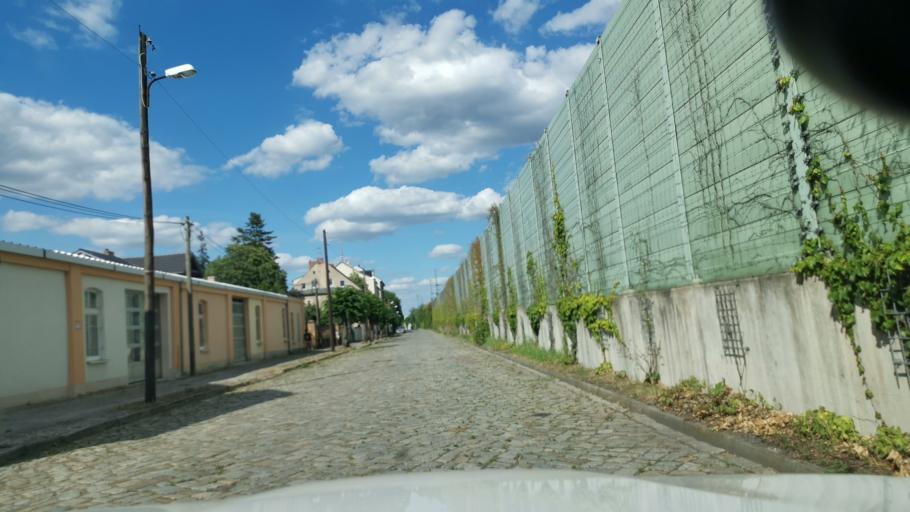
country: DE
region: Brandenburg
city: Luckenwalde
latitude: 52.0870
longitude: 13.1557
